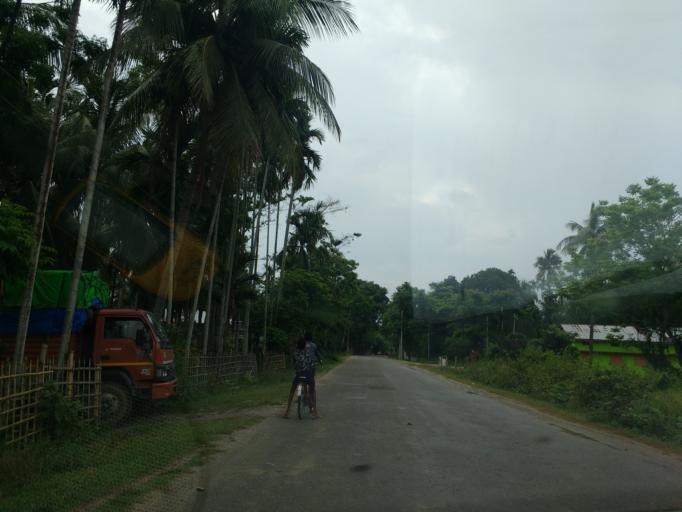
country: IN
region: Assam
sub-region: Udalguri
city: Udalguri
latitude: 26.7278
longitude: 92.2122
